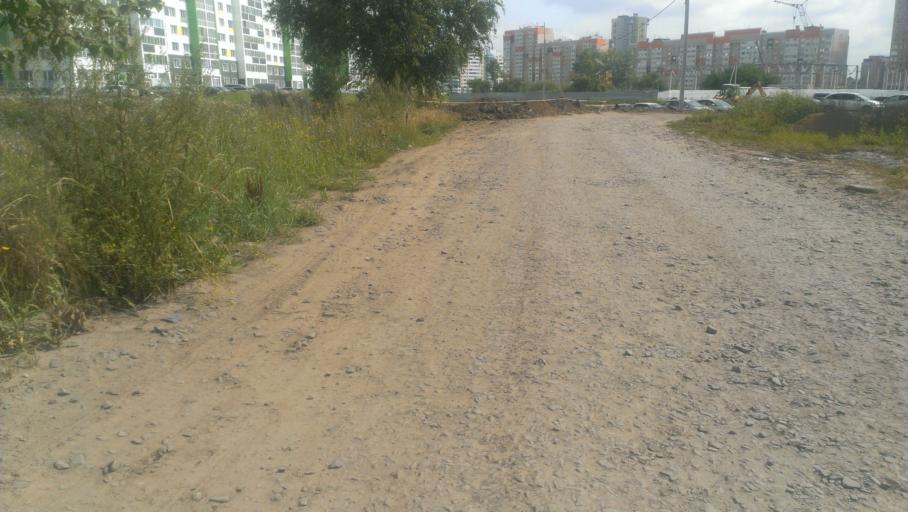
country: RU
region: Altai Krai
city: Novosilikatnyy
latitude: 53.3377
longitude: 83.6485
